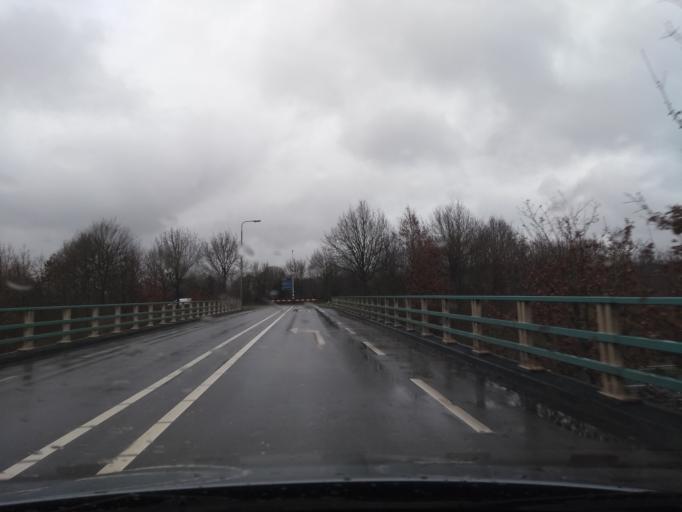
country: NL
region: Overijssel
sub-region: Gemeente Steenwijkerland
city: Tuk
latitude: 52.8056
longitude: 6.0942
